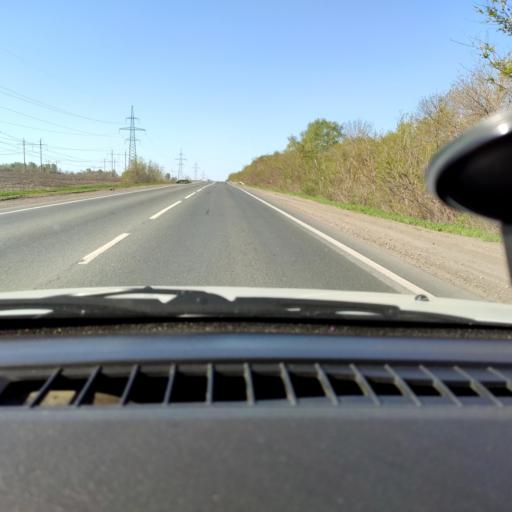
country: RU
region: Samara
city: Dubovyy Umet
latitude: 53.0791
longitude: 50.3885
